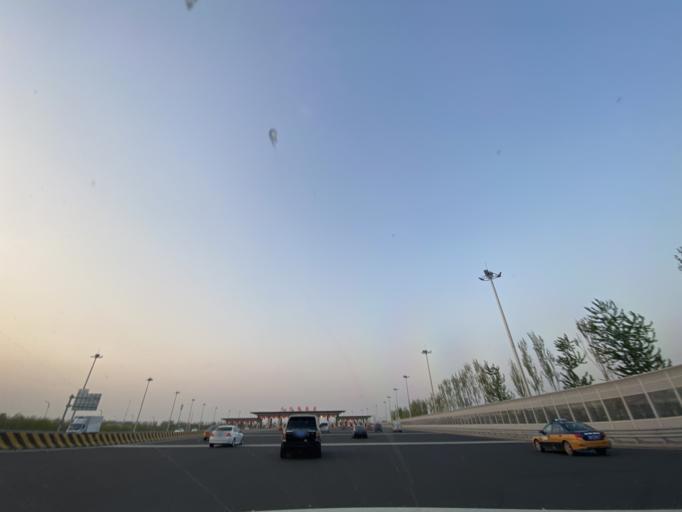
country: CN
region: Beijing
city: Xingfeng
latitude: 39.7248
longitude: 116.3789
